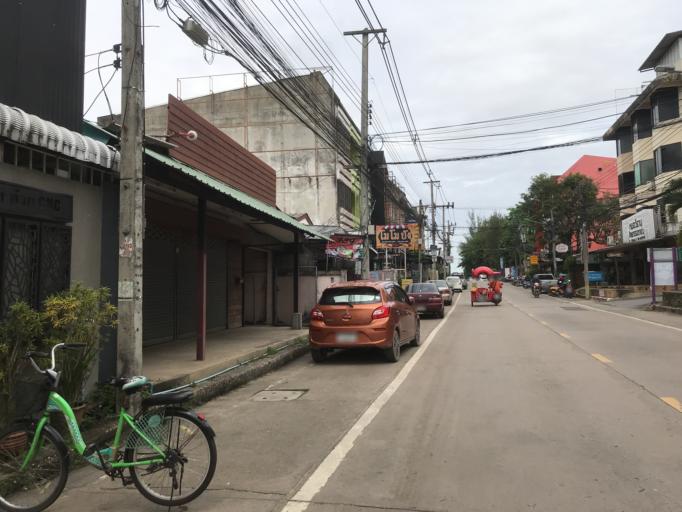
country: TH
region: Chiang Rai
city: Chiang Rai
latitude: 19.9027
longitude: 99.8157
